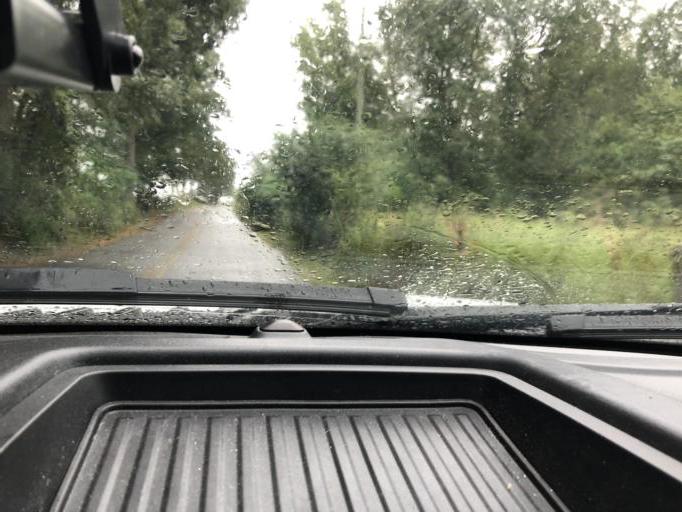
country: US
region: Georgia
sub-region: Putnam County
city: Jefferson
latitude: 33.3882
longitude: -83.2568
